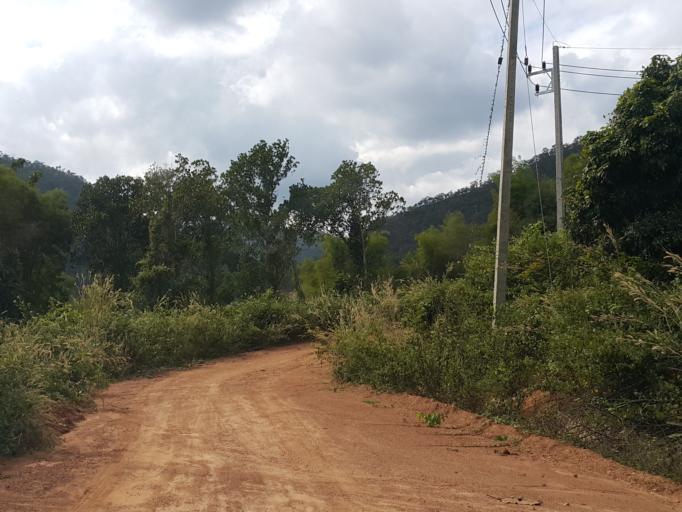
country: TH
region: Lampang
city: Chae Hom
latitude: 18.5748
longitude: 99.4437
